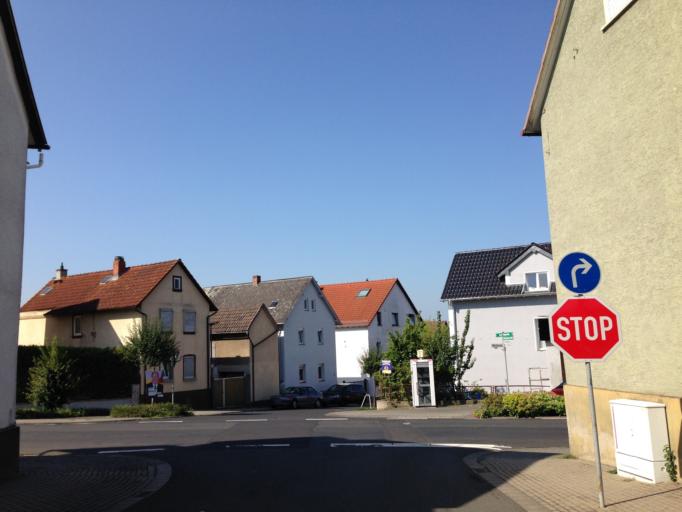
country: DE
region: Hesse
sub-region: Regierungsbezirk Giessen
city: Hoernsheim
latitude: 50.5319
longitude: 8.6511
